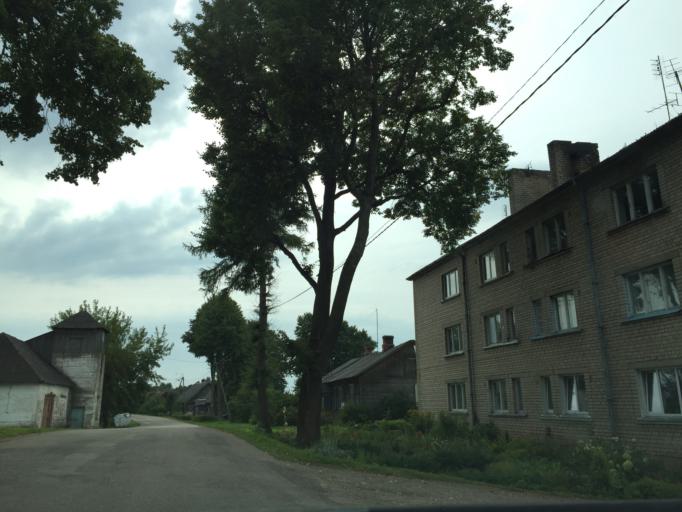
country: LV
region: Zilupes
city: Zilupe
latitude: 56.2612
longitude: 27.9870
